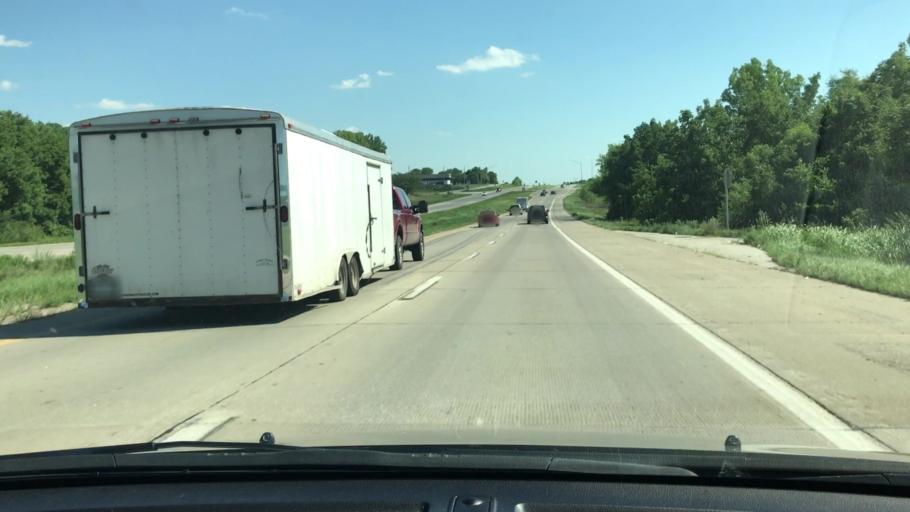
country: US
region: Missouri
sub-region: Jackson County
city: Lees Summit
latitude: 38.8819
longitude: -94.3739
